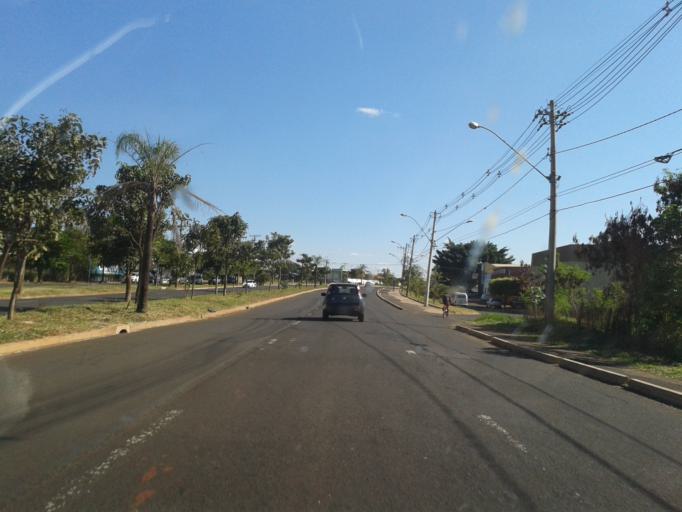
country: BR
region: Minas Gerais
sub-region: Uberaba
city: Uberaba
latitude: -19.7481
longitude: -47.9699
